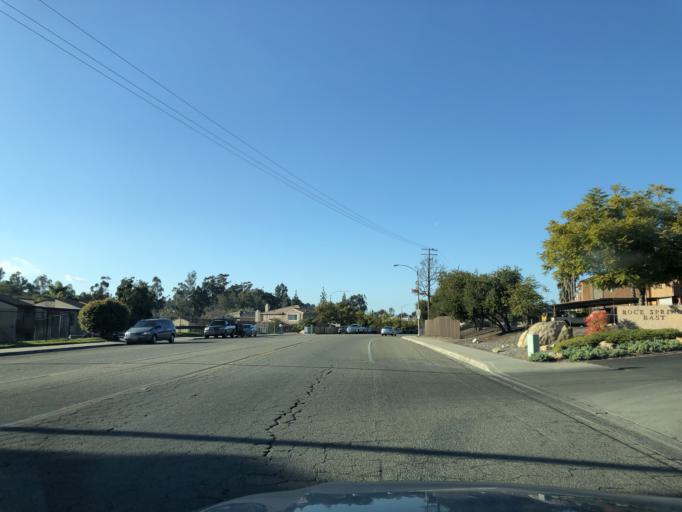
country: US
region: California
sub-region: San Diego County
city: Escondido
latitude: 33.1303
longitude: -117.0994
